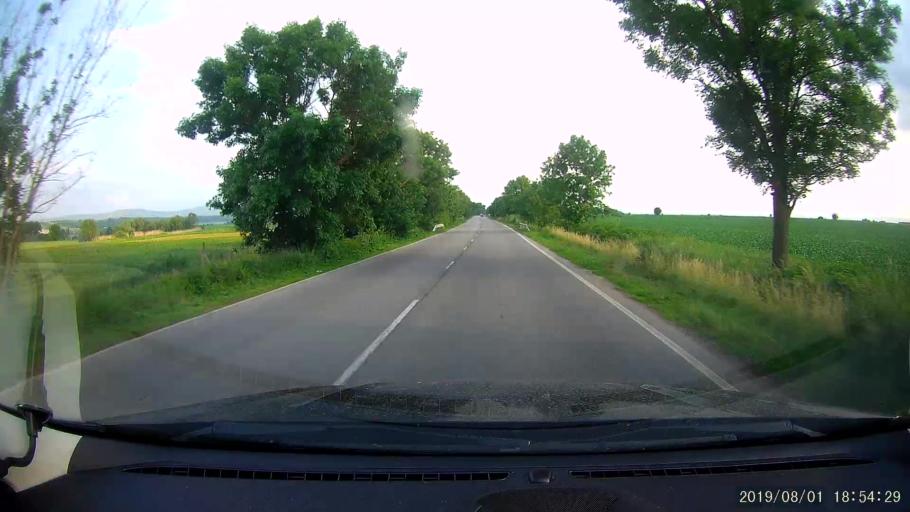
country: BG
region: Shumen
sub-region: Obshtina Shumen
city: Shumen
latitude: 43.1976
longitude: 27.0020
